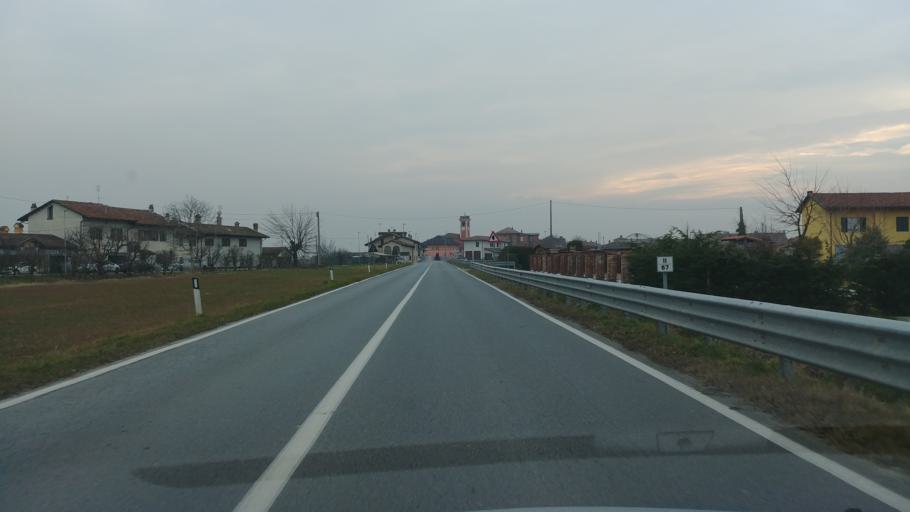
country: IT
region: Piedmont
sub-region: Provincia di Cuneo
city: Sant'Albano Stura
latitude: 44.5138
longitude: 7.6916
